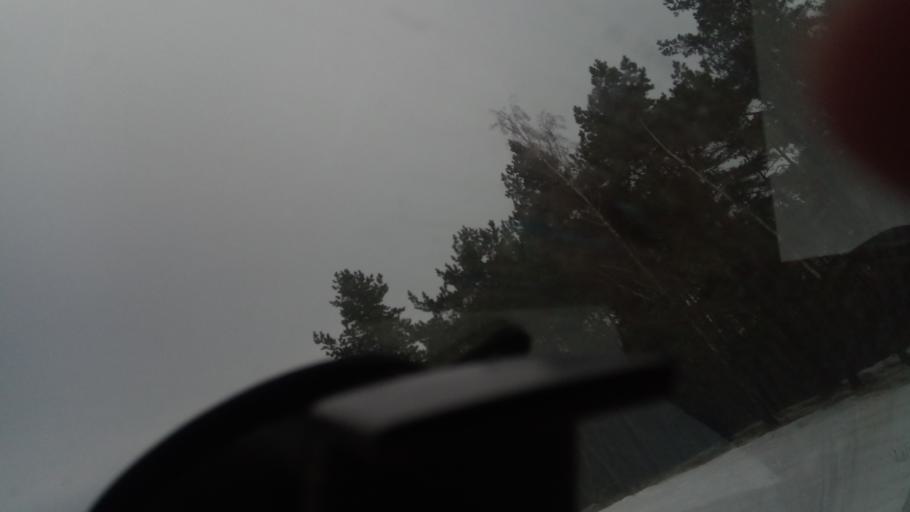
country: LT
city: Neringa
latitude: 55.4228
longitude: 21.1076
